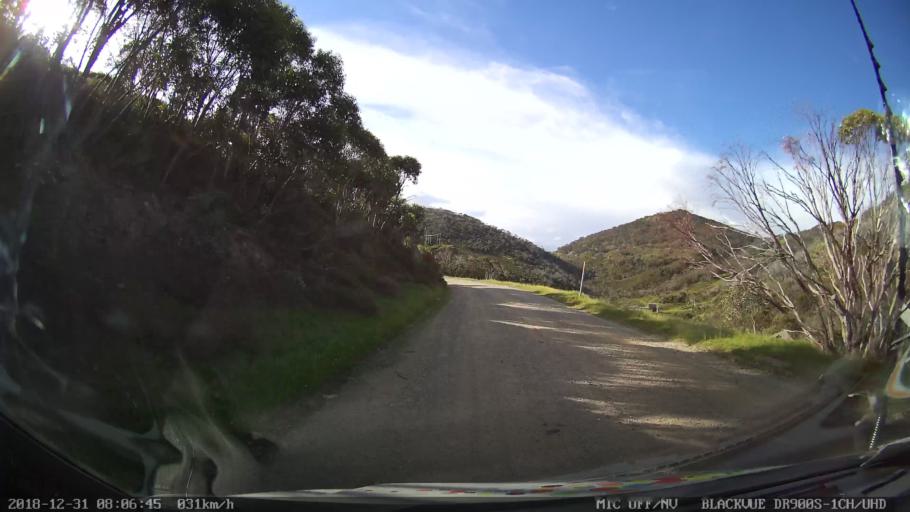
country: AU
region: New South Wales
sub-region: Snowy River
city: Jindabyne
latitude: -36.3757
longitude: 148.4084
